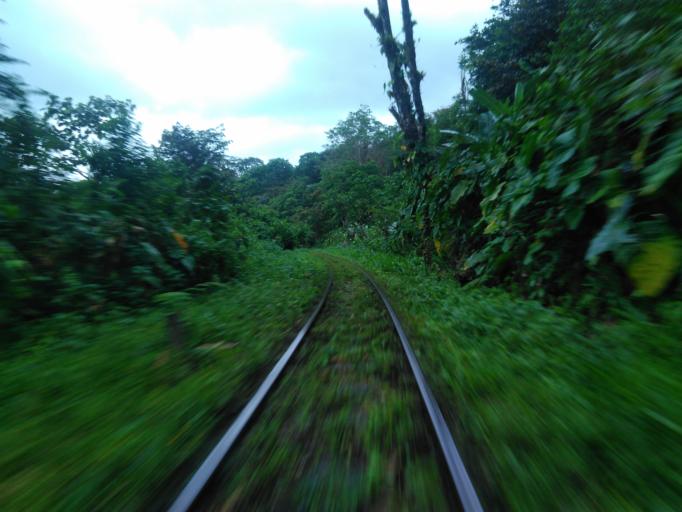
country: CO
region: Valle del Cauca
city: Buenaventura
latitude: 3.8403
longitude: -76.8711
